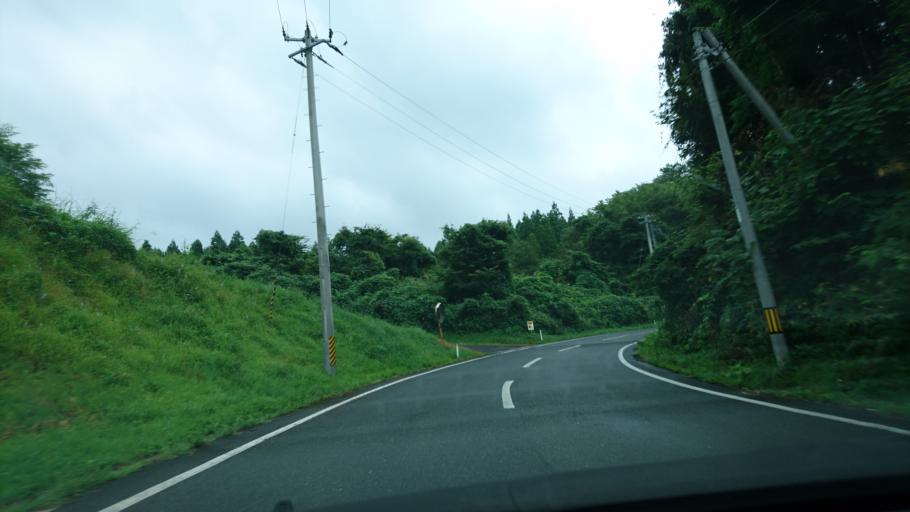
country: JP
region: Iwate
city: Ichinoseki
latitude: 38.8910
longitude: 140.9615
